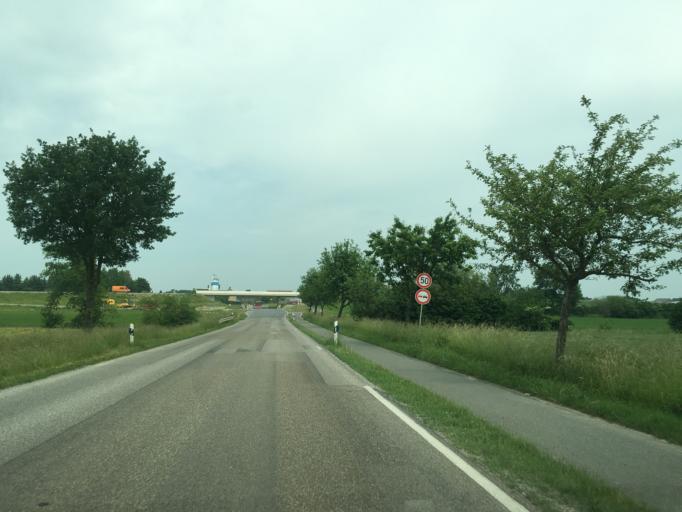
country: DE
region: North Rhine-Westphalia
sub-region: Regierungsbezirk Munster
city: Nordwalde
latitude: 52.0741
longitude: 7.4792
